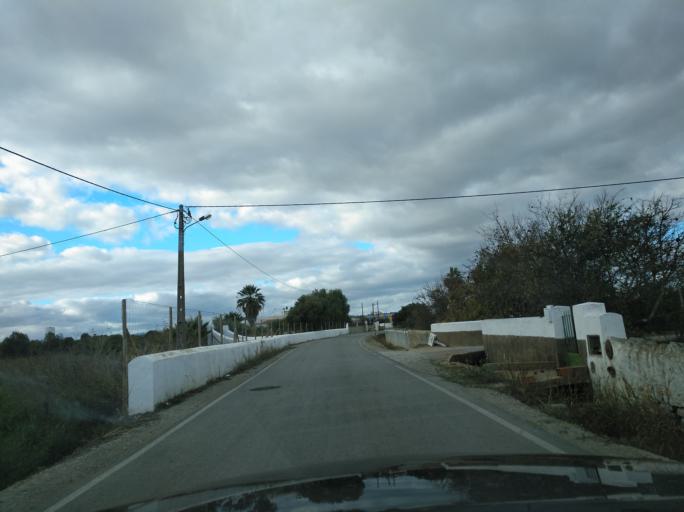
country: PT
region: Faro
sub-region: Tavira
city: Luz
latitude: 37.0979
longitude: -7.7064
